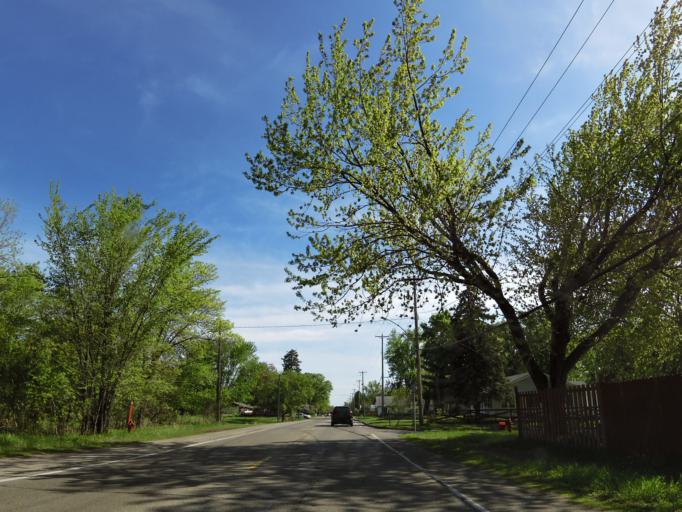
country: US
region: Minnesota
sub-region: Ramsey County
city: North Saint Paul
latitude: 45.0116
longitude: -92.9848
